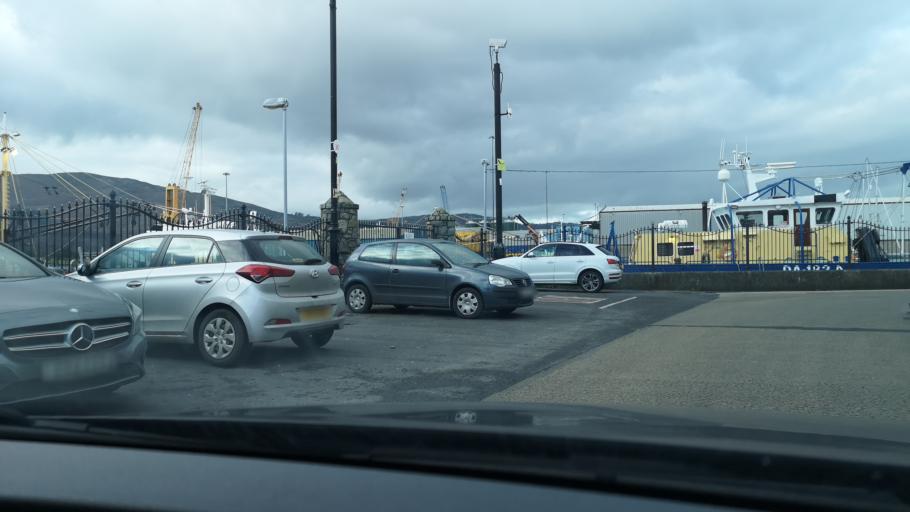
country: GB
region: Northern Ireland
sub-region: Down District
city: Warrenpoint
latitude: 54.0996
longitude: -6.2552
